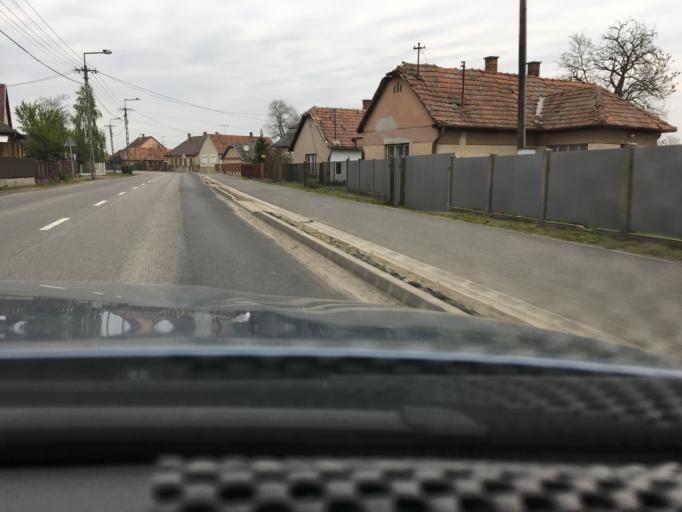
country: HU
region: Hajdu-Bihar
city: Hajdusamson
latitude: 47.6039
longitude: 21.7628
